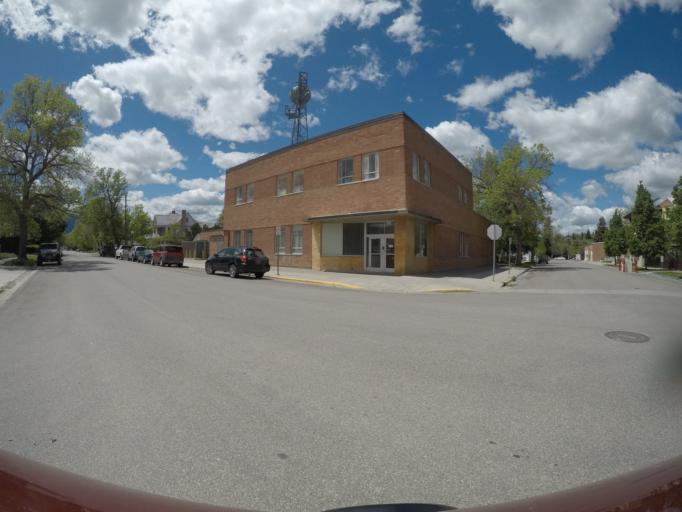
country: US
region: Montana
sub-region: Park County
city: Livingston
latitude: 45.6601
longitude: -110.5623
